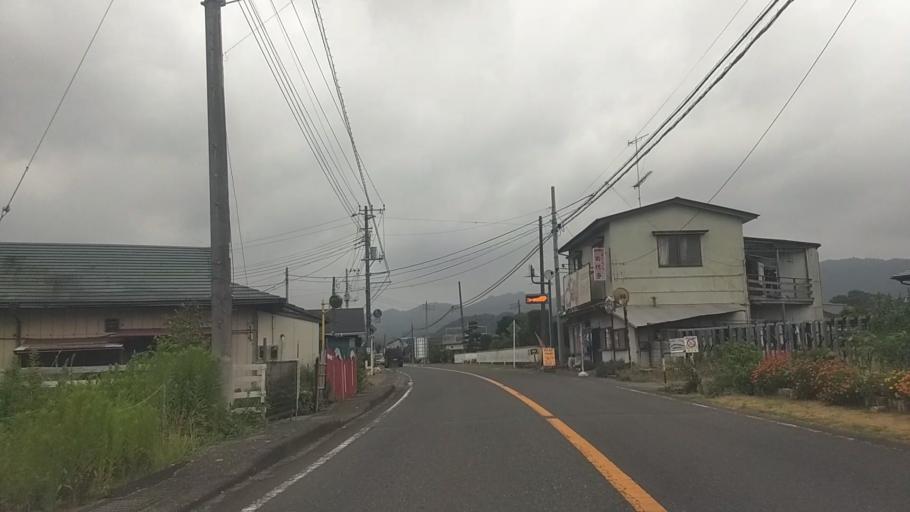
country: JP
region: Chiba
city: Kawaguchi
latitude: 35.1332
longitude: 140.0067
